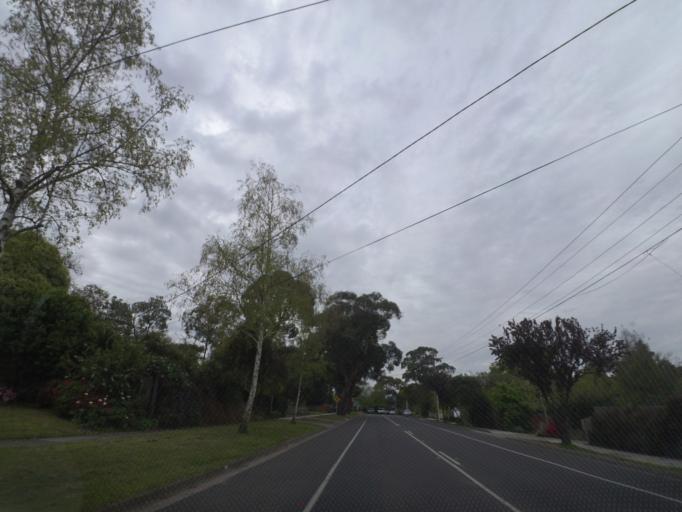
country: AU
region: Victoria
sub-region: Knox
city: The Basin
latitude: -37.8515
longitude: 145.3025
